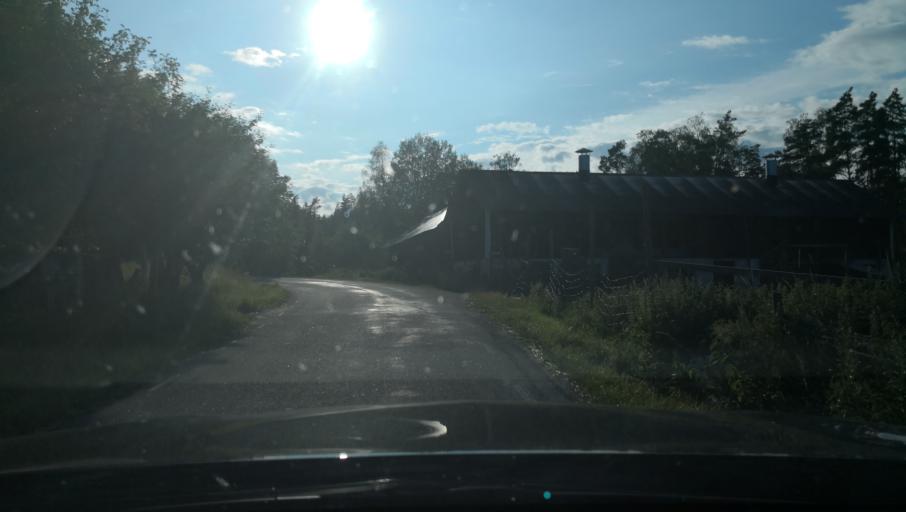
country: SE
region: Uppsala
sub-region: Osthammars Kommun
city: Osterbybruk
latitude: 60.0174
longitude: 17.9324
